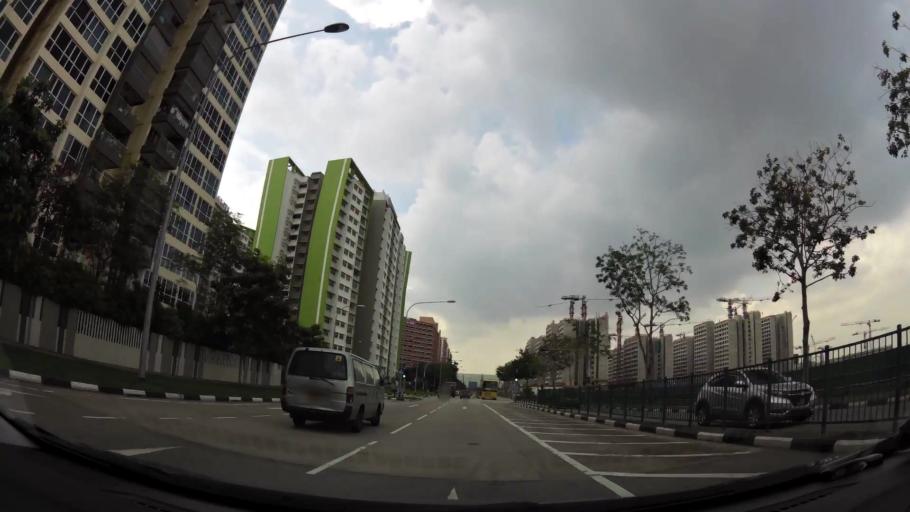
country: SG
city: Singapore
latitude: 1.3603
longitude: 103.9398
